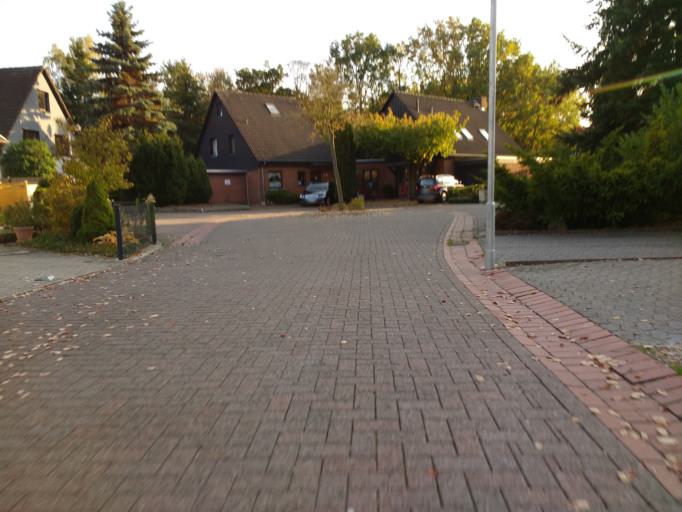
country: DE
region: Lower Saxony
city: Gifhorn
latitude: 52.4638
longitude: 10.5481
